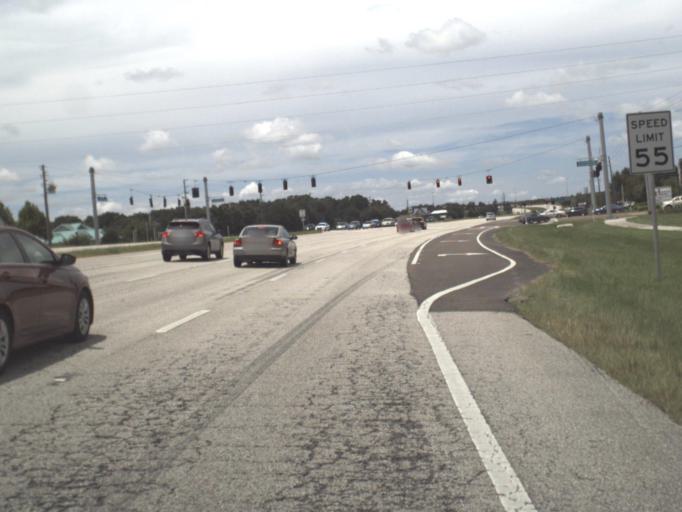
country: US
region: Florida
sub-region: Hillsborough County
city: Pebble Creek
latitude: 28.1865
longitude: -82.3733
